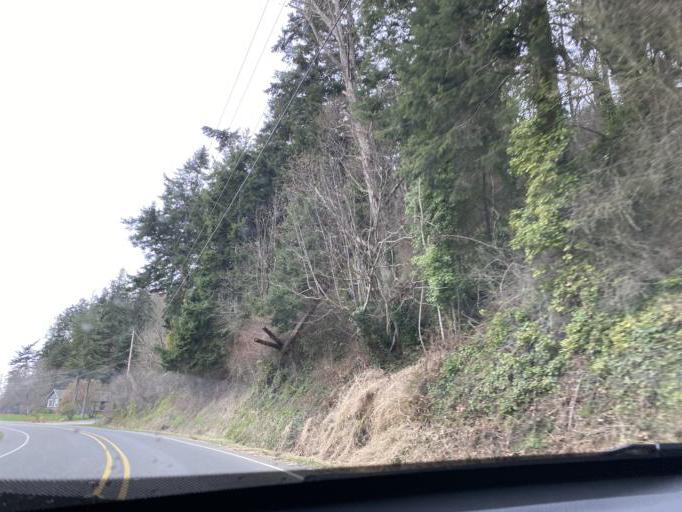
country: US
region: Washington
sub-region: Island County
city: Freeland
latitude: 47.9888
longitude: -122.5124
